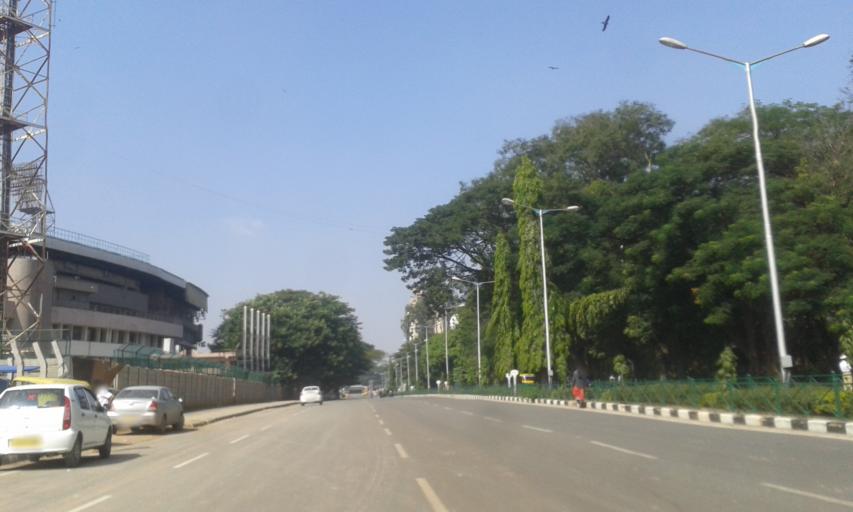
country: IN
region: Karnataka
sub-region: Bangalore Urban
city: Bangalore
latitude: 12.9795
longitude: 77.6012
